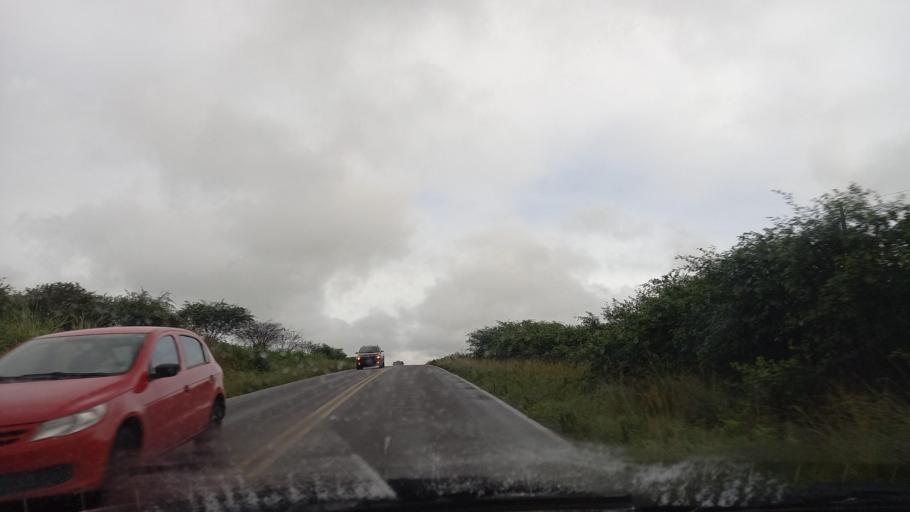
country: BR
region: Pernambuco
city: Garanhuns
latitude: -8.8450
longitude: -36.5258
